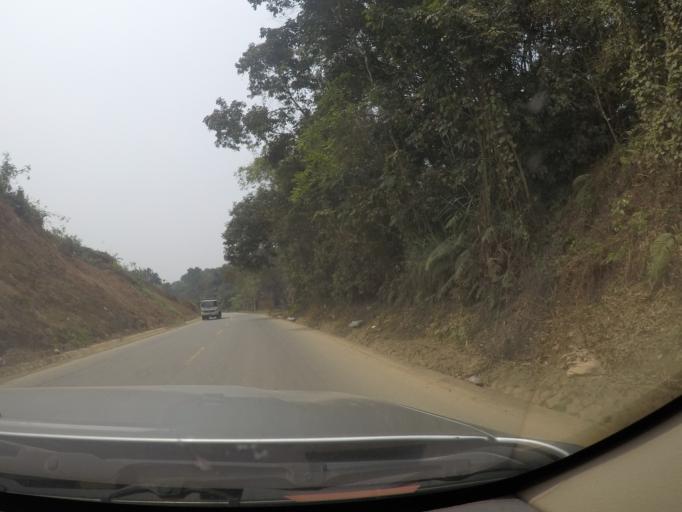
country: VN
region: Thanh Hoa
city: Thi Tran Ngoc Lac
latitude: 20.1239
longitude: 105.3875
